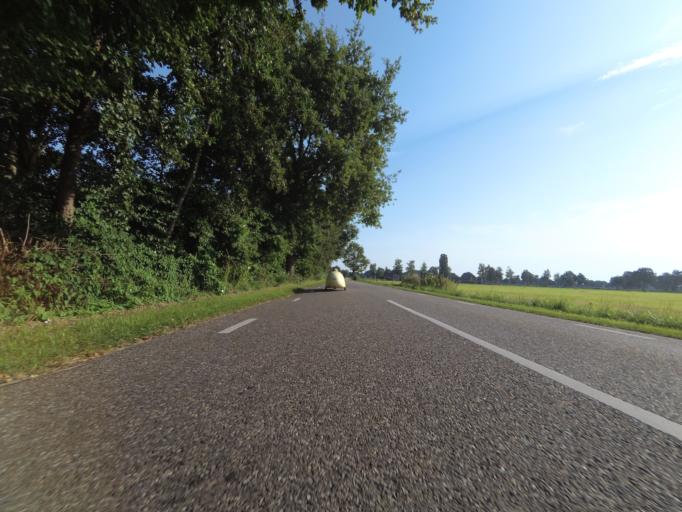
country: NL
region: Gelderland
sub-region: Gemeente Epe
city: Vaassen
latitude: 52.2481
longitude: 5.9609
